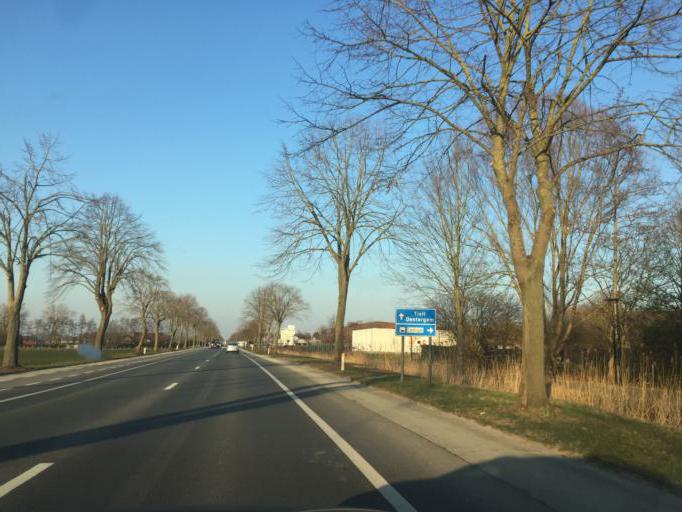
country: BE
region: Flanders
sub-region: Provincie West-Vlaanderen
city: Meulebeke
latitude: 50.9579
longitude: 3.2916
